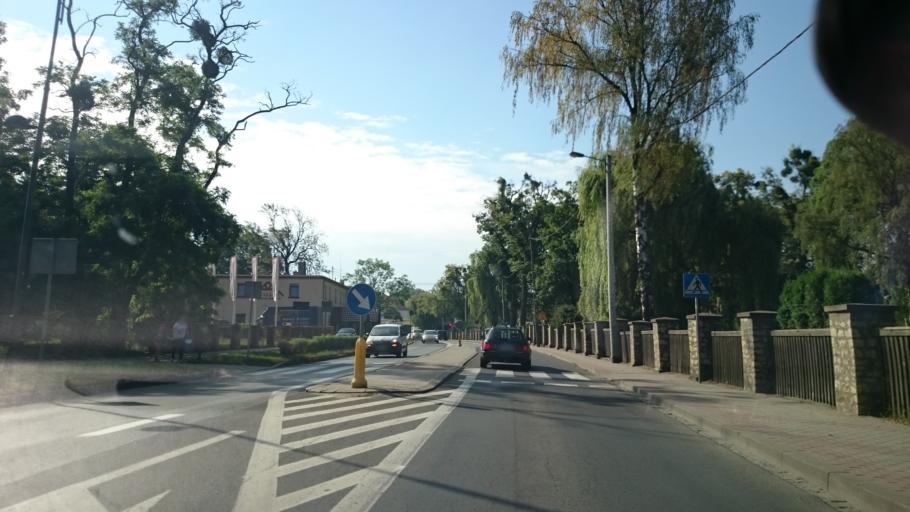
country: PL
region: Opole Voivodeship
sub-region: Powiat strzelecki
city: Strzelce Opolskie
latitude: 50.5136
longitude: 18.2913
